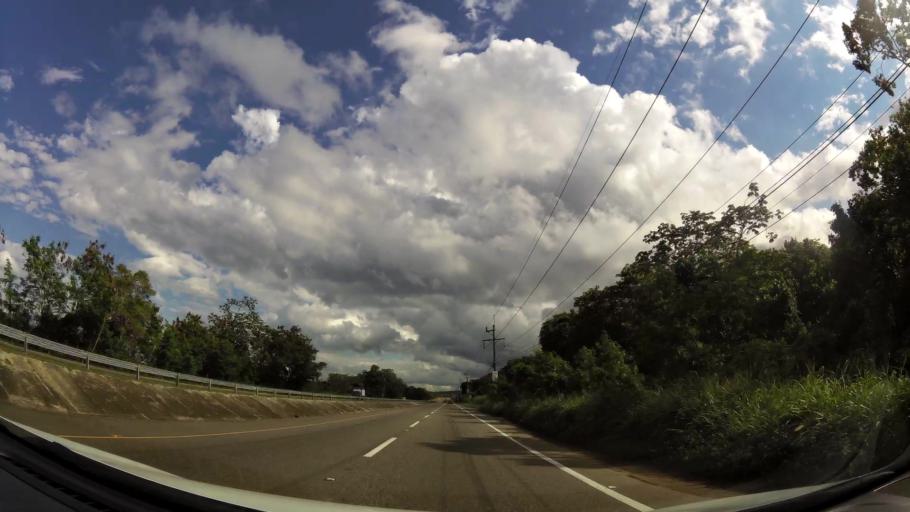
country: DO
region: La Vega
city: Concepcion de La Vega
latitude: 19.1754
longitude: -70.4939
